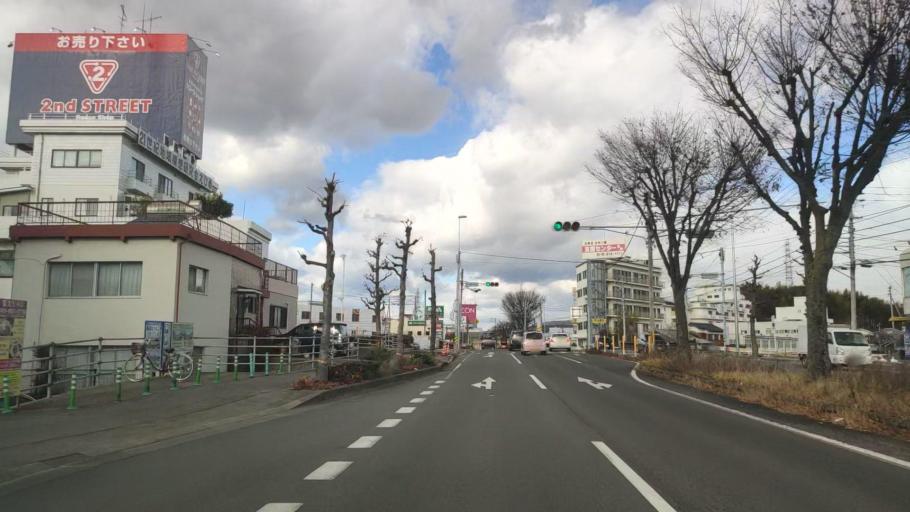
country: JP
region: Ehime
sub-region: Shikoku-chuo Shi
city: Matsuyama
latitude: 33.8171
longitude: 132.7770
